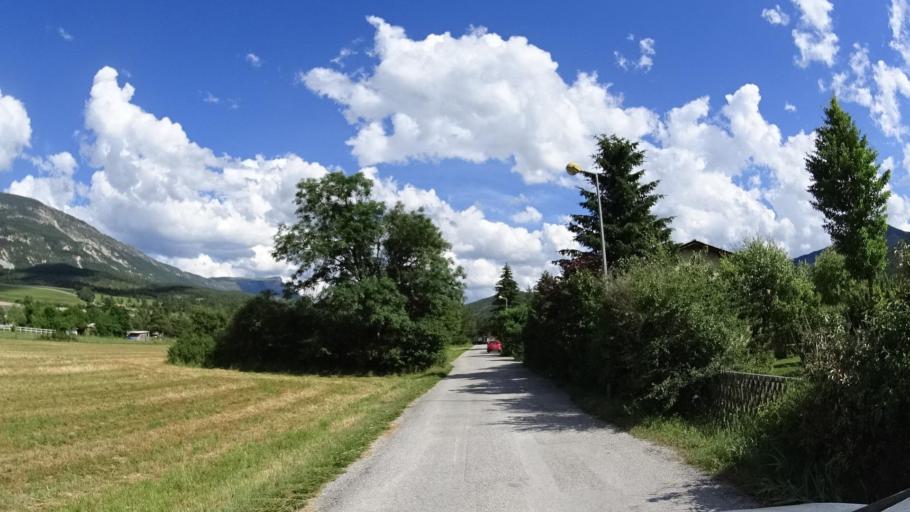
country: FR
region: Provence-Alpes-Cote d'Azur
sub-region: Departement des Alpes-de-Haute-Provence
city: Castellane
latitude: 43.9639
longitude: 6.5090
